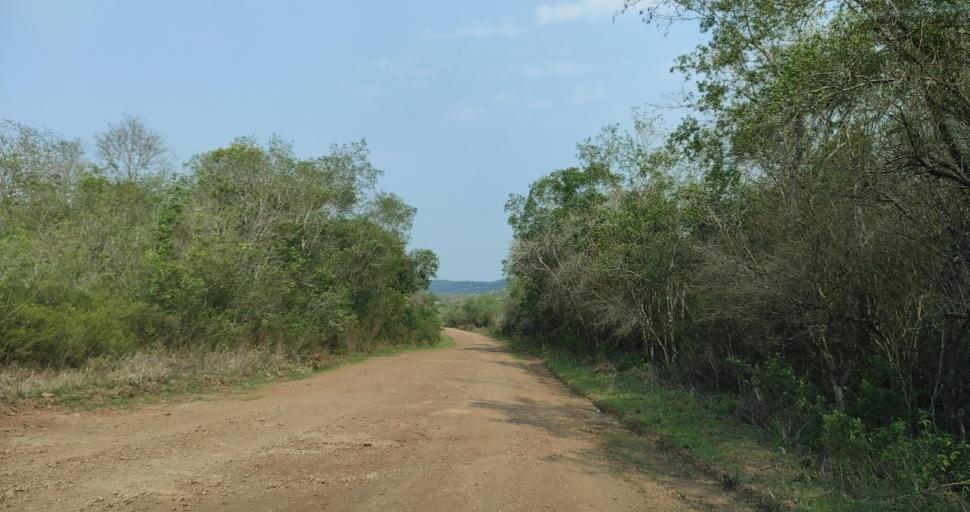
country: AR
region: Misiones
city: Cerro Cora
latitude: -27.5891
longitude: -55.5798
